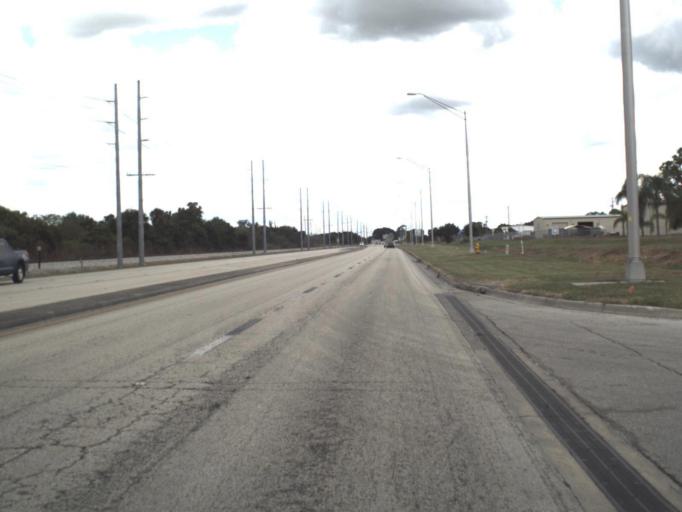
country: US
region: Florida
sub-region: Polk County
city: Mulberry
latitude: 27.8945
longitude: -81.9515
